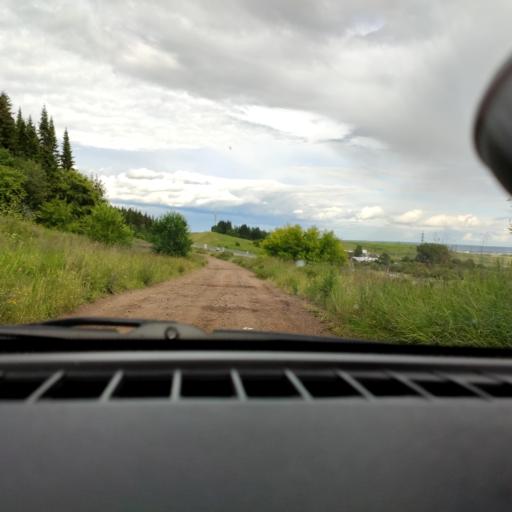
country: RU
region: Perm
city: Froly
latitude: 57.9357
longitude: 56.2102
